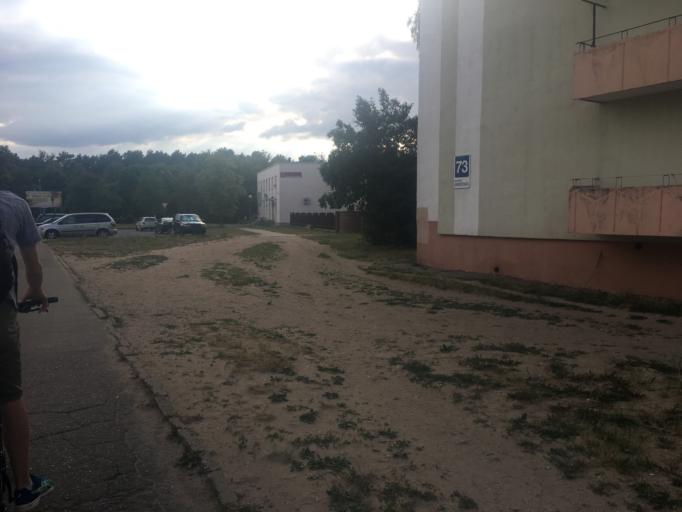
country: BY
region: Grodnenskaya
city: Hrodna
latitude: 53.6902
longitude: 23.8032
